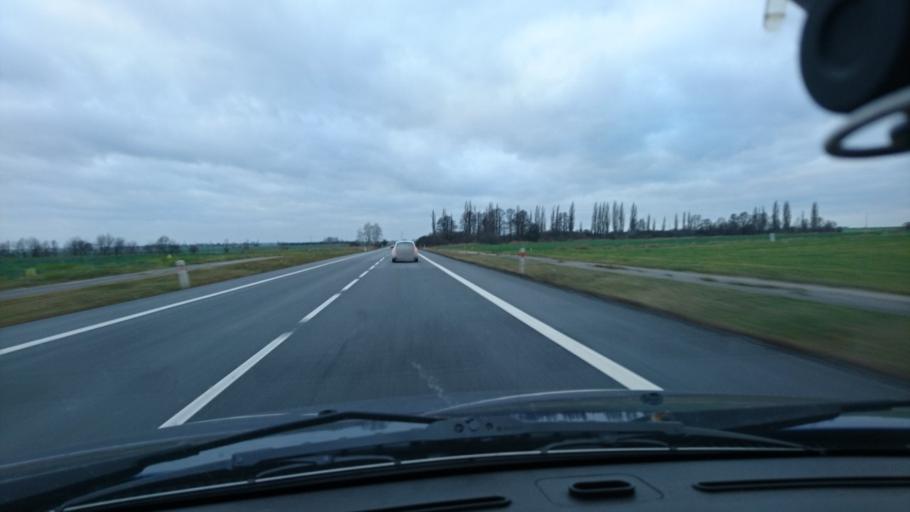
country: PL
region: Opole Voivodeship
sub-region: Powiat kluczborski
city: Kluczbork
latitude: 50.9831
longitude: 18.2436
